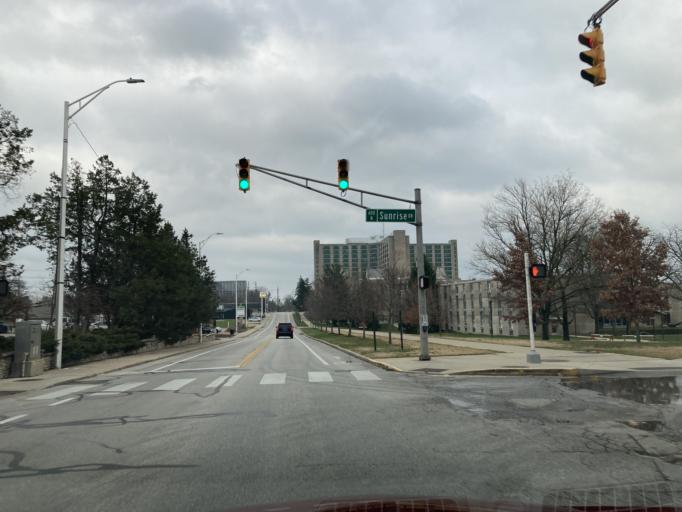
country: US
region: Indiana
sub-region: Monroe County
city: Bloomington
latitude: 39.1716
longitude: -86.5126
